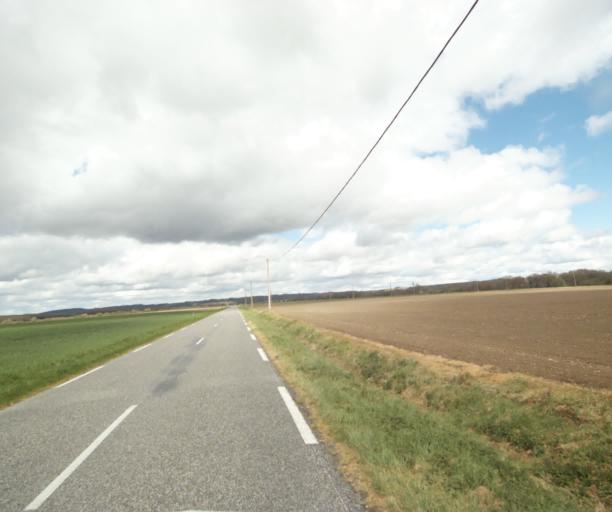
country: FR
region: Midi-Pyrenees
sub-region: Departement de l'Ariege
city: Mazeres
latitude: 43.2453
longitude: 1.6371
